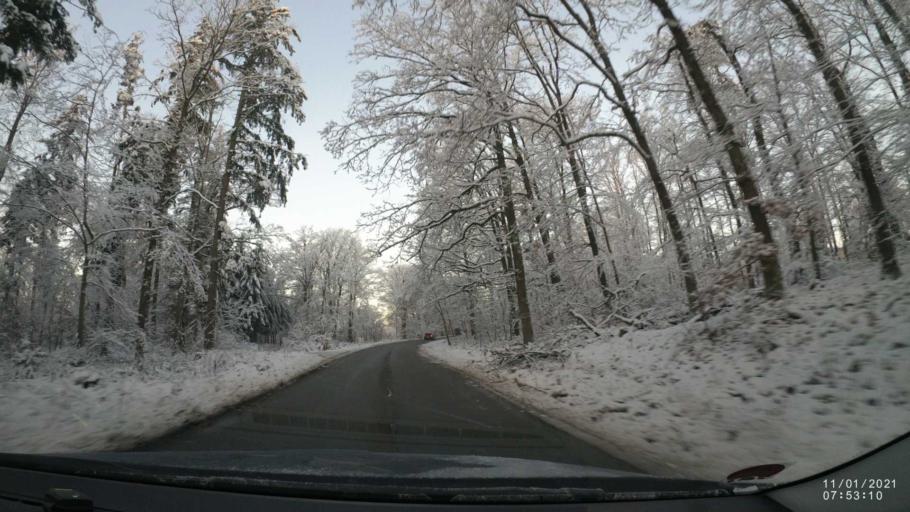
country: CZ
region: South Moravian
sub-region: Okres Blansko
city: Adamov
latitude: 49.2908
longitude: 16.6374
